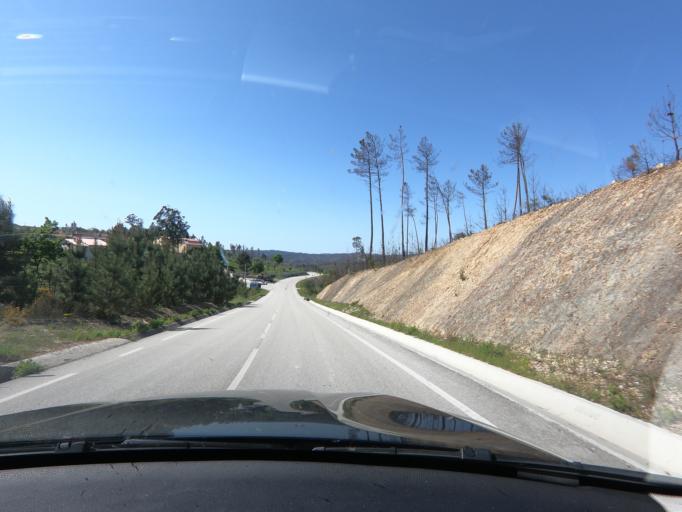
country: PT
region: Coimbra
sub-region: Penacova
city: Penacova
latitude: 40.2866
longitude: -8.2407
